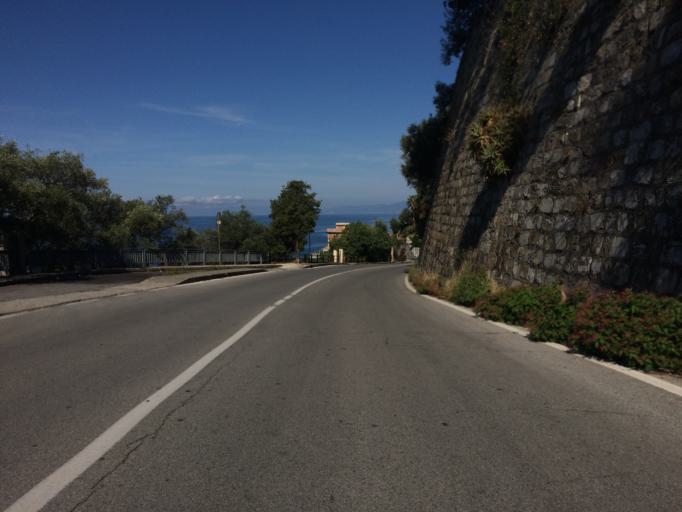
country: IT
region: Liguria
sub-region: Provincia di Genova
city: Recco
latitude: 44.3566
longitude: 9.1498
